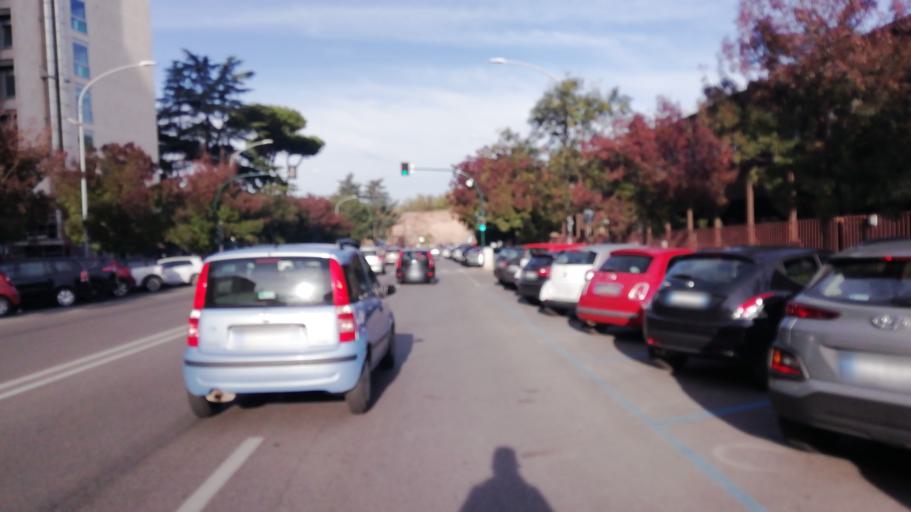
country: IT
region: Latium
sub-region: Citta metropolitana di Roma Capitale
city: Rome
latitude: 41.8753
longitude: 12.4847
